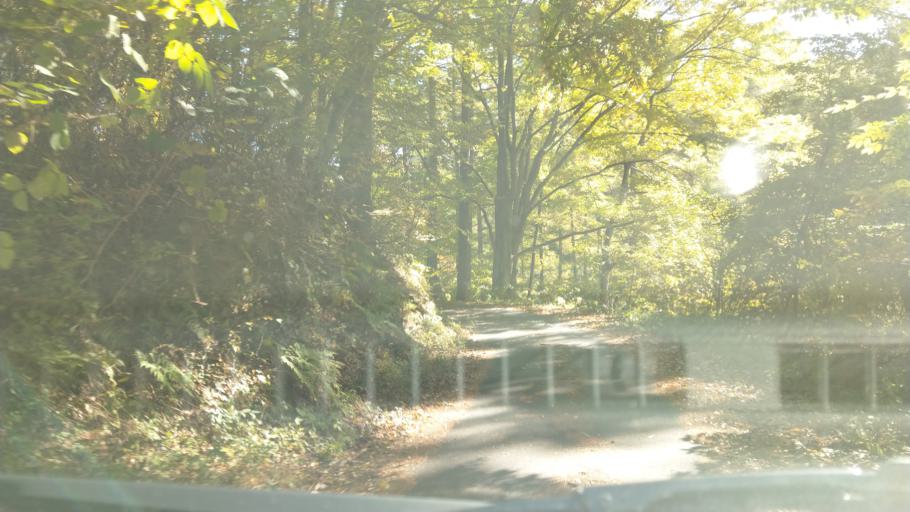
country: JP
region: Nagano
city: Komoro
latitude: 36.3797
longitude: 138.4285
